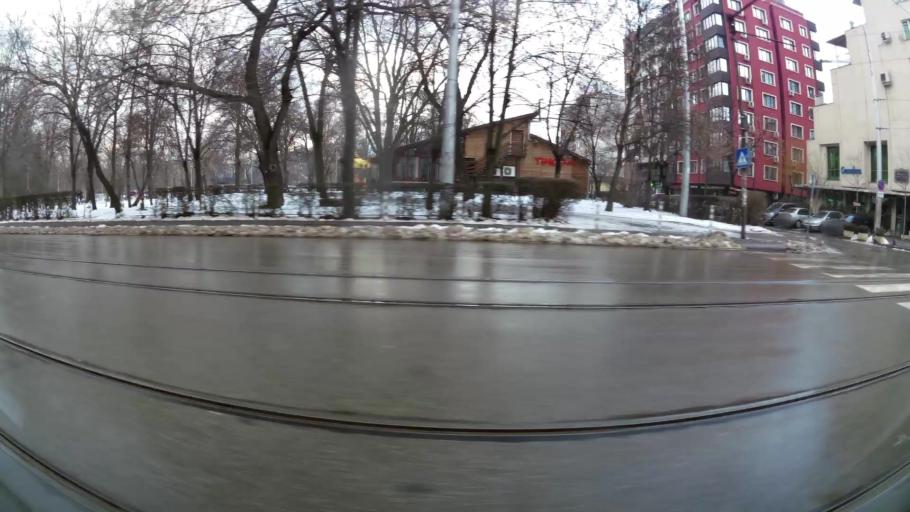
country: BG
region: Sofia-Capital
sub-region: Stolichna Obshtina
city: Sofia
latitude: 42.7059
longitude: 23.2942
